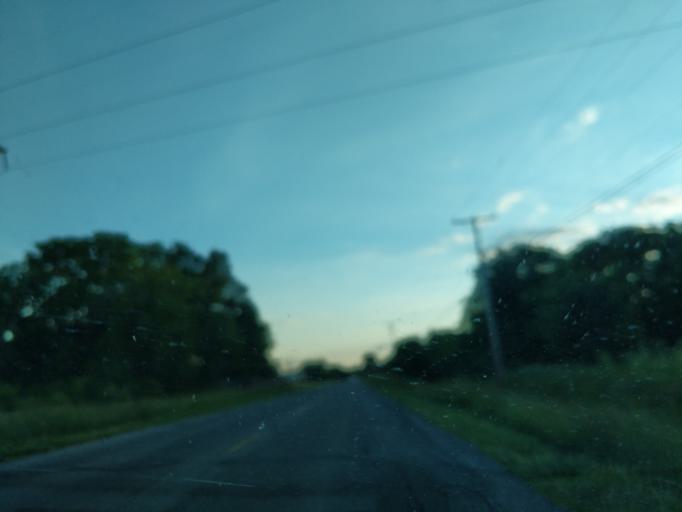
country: US
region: Indiana
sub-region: Madison County
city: Chesterfield
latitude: 40.1119
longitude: -85.5846
